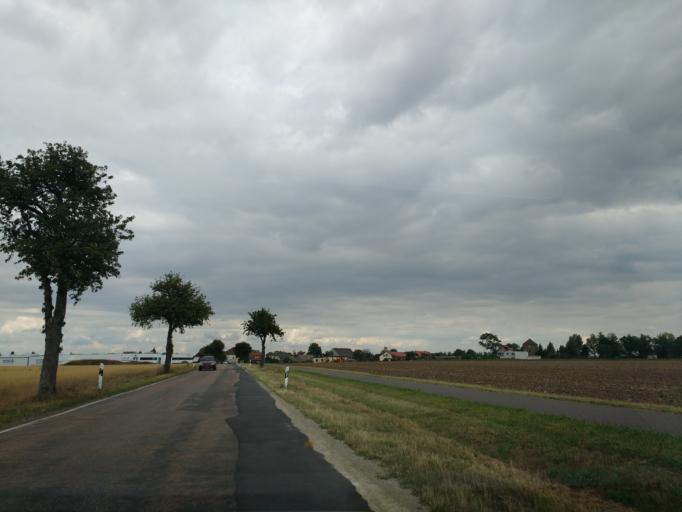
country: DE
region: Saxony-Anhalt
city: Dolbau
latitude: 51.4545
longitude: 12.0604
